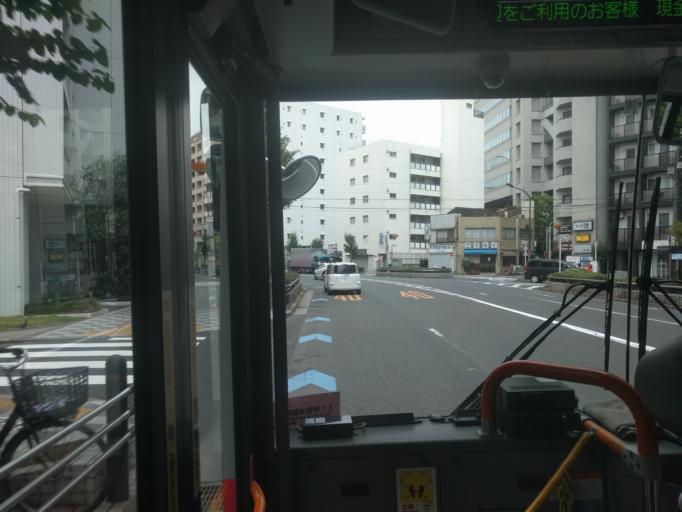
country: JP
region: Kanagawa
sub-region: Kawasaki-shi
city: Kawasaki
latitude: 35.5610
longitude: 139.7197
